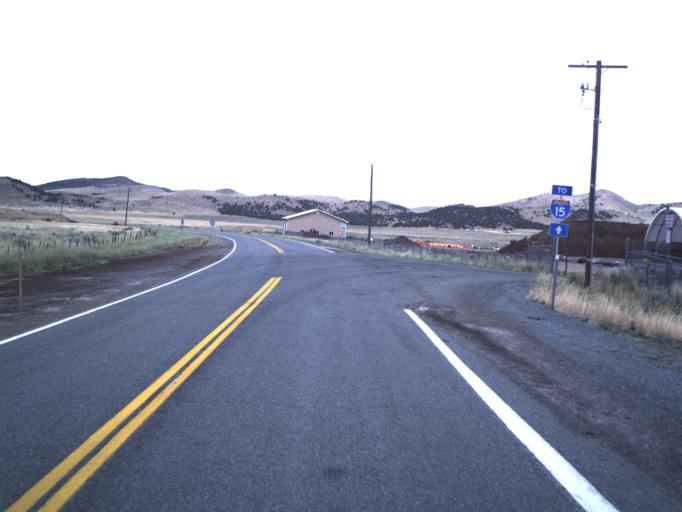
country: US
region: Utah
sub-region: Beaver County
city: Beaver
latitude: 38.6022
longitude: -112.5822
